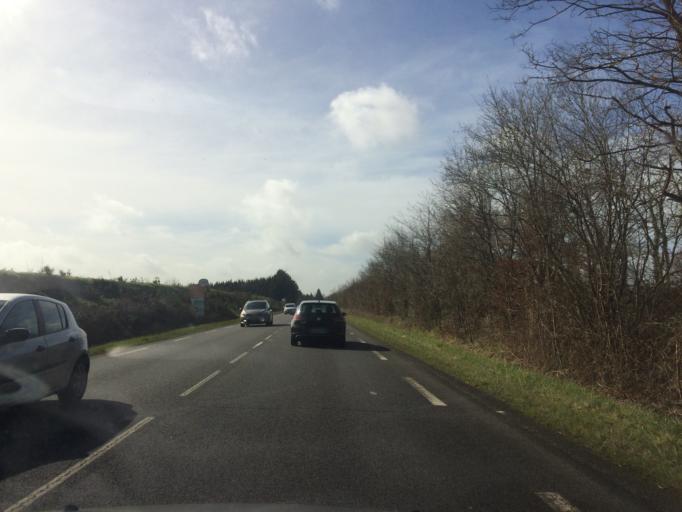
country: FR
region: Pays de la Loire
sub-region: Departement de la Loire-Atlantique
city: Besne
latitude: 47.3975
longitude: -2.0968
